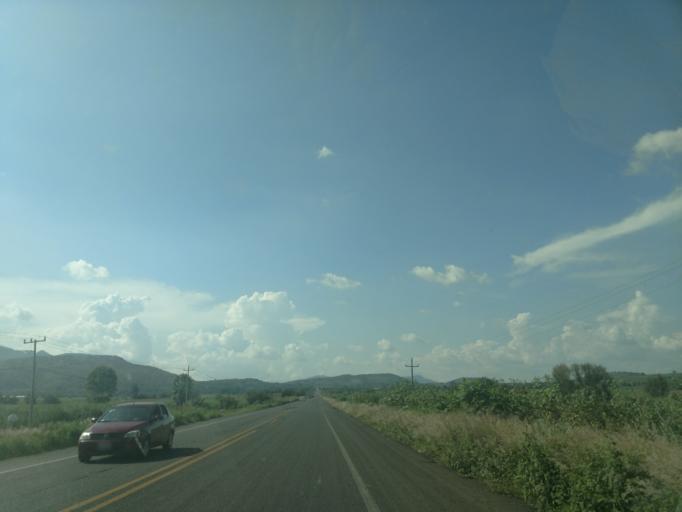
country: MX
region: Jalisco
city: Ahualulco de Mercado
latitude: 20.7194
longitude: -103.9812
